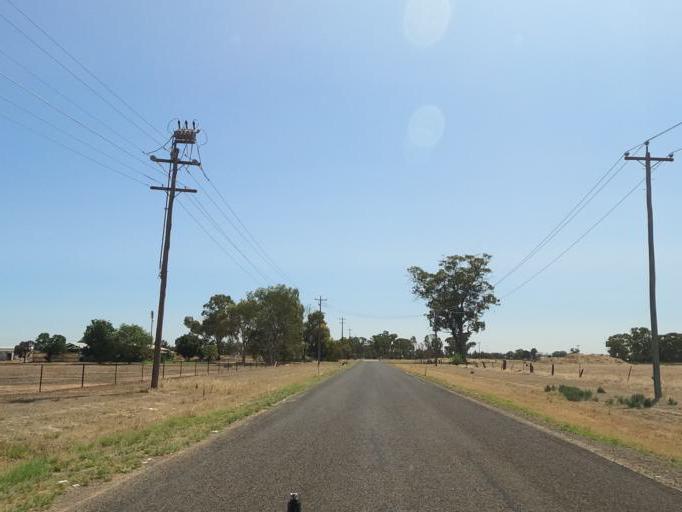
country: AU
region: New South Wales
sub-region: Corowa Shire
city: Mulwala
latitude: -35.9802
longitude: 146.0038
